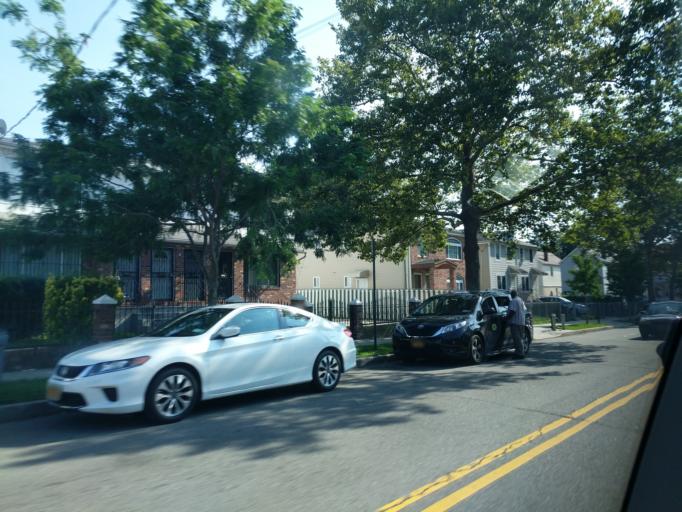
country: US
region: New York
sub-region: Queens County
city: Jamaica
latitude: 40.6929
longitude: -73.7900
